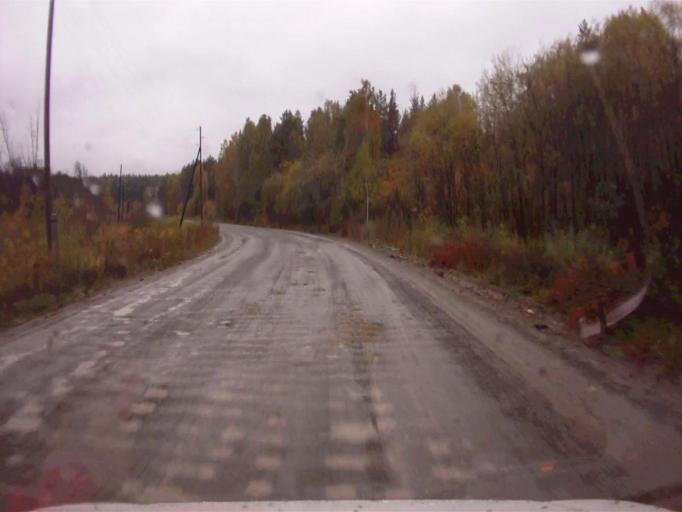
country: RU
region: Chelyabinsk
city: Kyshtym
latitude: 55.7424
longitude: 60.5048
